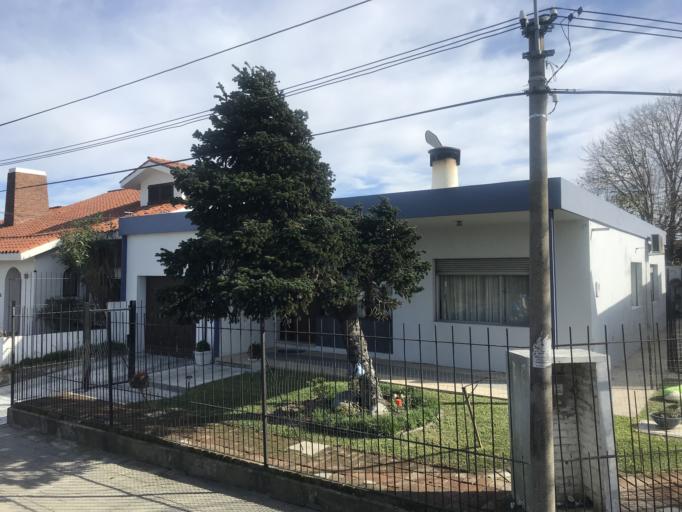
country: UY
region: Colonia
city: Colonia del Sacramento
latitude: -34.4682
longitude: -57.8384
